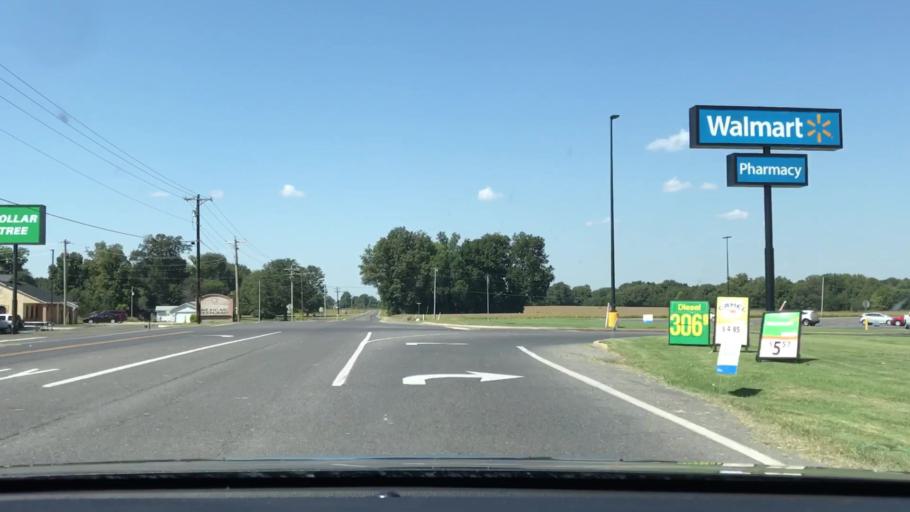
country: US
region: Kentucky
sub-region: Fulton County
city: Fulton
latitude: 36.5156
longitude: -88.8998
